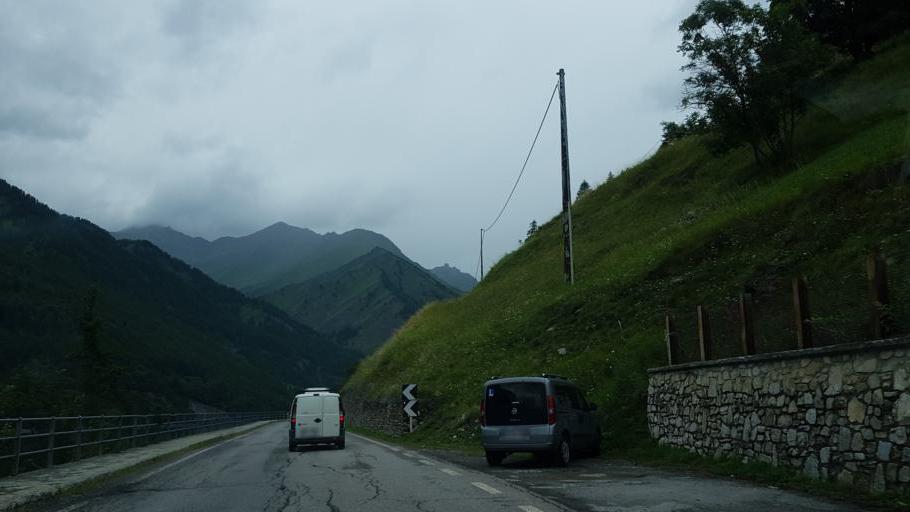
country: IT
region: Piedmont
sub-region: Provincia di Cuneo
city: Pontechianale
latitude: 44.6155
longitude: 7.0477
